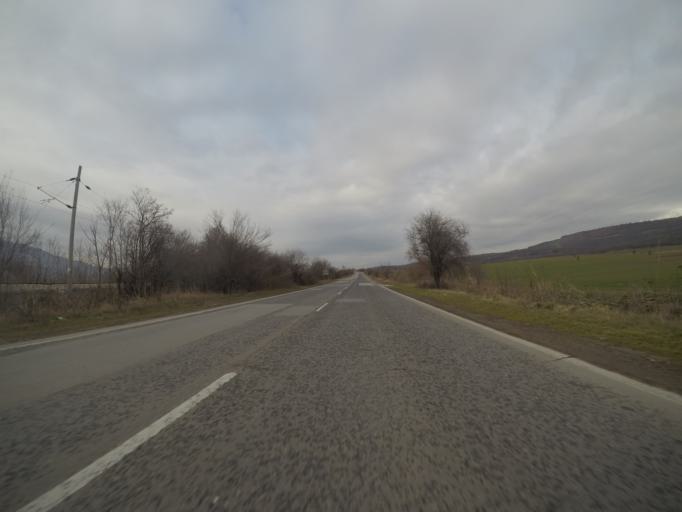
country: BG
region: Kyustendil
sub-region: Obshtina Boboshevo
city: Boboshevo
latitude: 42.1244
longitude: 23.0393
